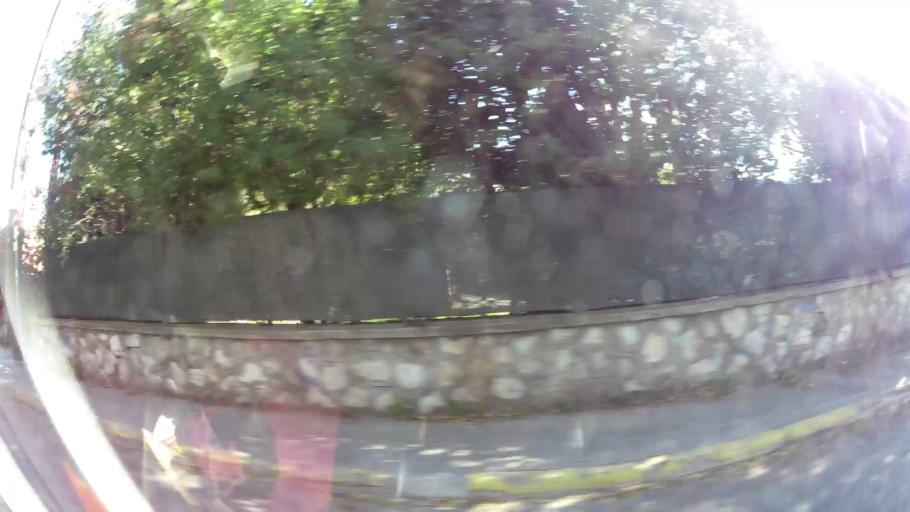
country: GR
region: Attica
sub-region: Nomarchia Athinas
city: Lykovrysi
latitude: 38.0751
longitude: 23.7939
